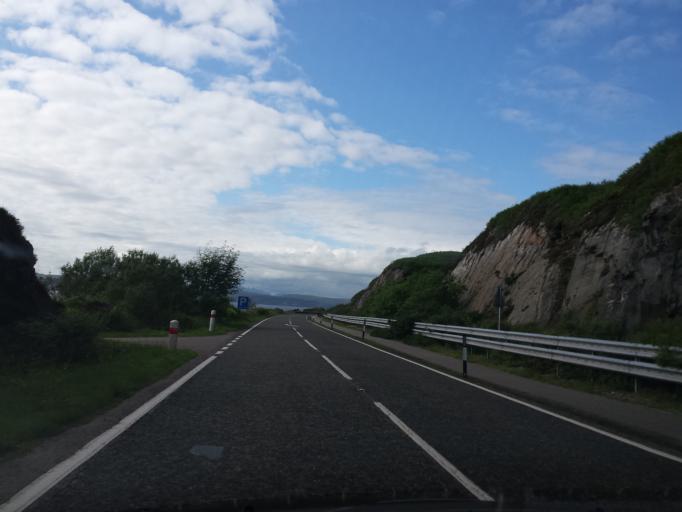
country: GB
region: Scotland
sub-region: Argyll and Bute
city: Isle Of Mull
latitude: 56.9935
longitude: -5.8299
